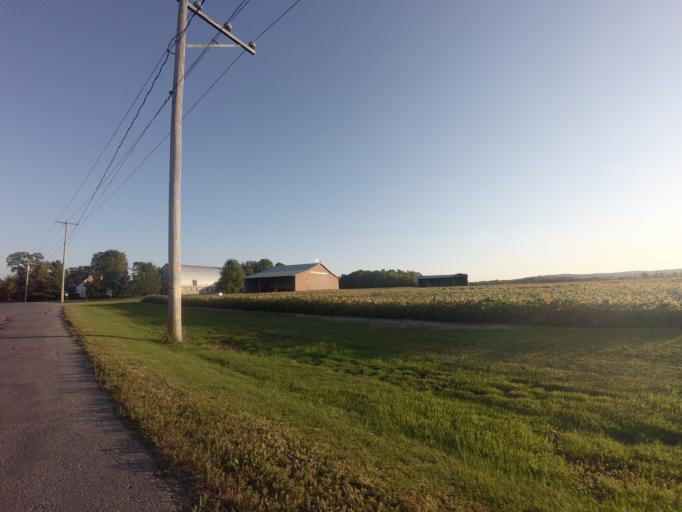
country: CA
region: Quebec
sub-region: Monteregie
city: Hudson
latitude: 45.4809
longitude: -74.2045
